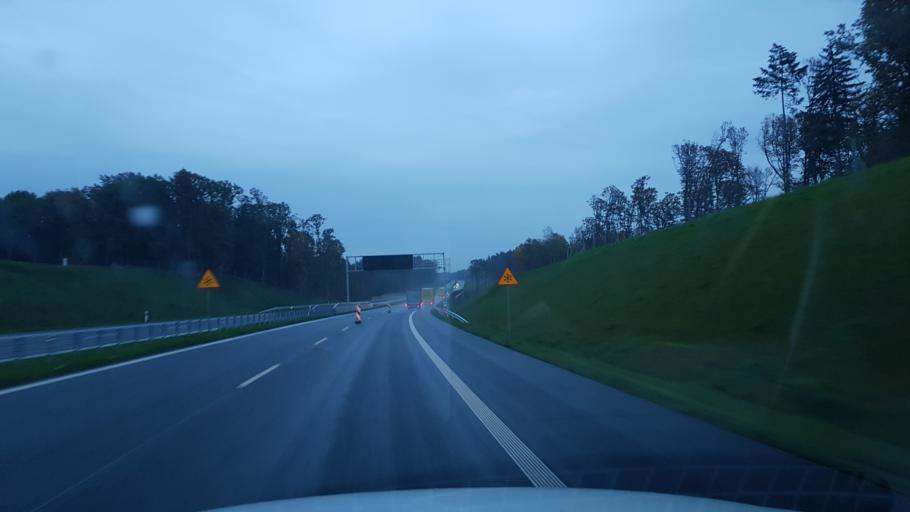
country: PL
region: West Pomeranian Voivodeship
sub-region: Powiat gryficki
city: Ploty
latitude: 53.8246
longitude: 15.2692
